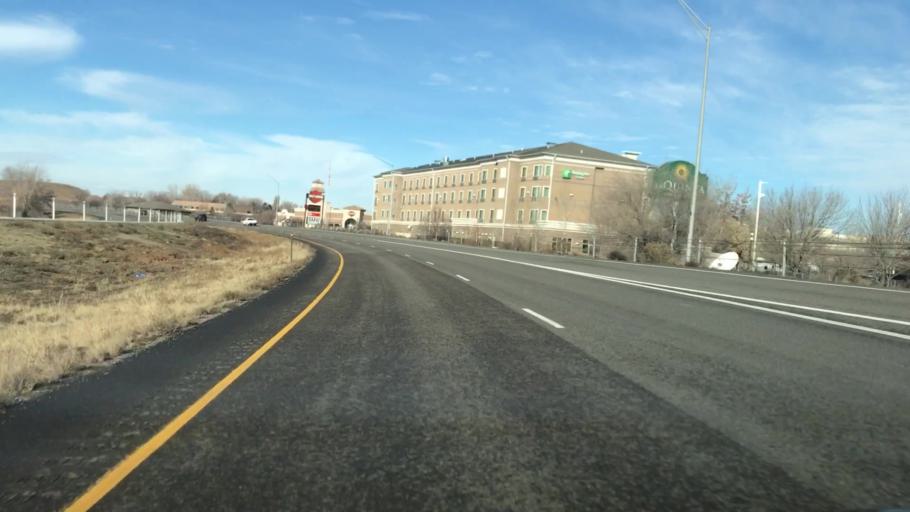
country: US
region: Colorado
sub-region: Mesa County
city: Grand Junction
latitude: 39.1140
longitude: -108.5415
